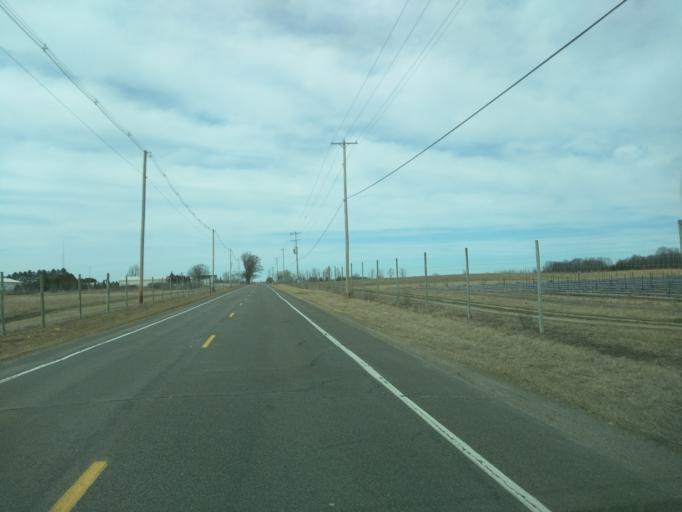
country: US
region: Michigan
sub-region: Ingham County
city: Holt
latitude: 42.6705
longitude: -84.4840
